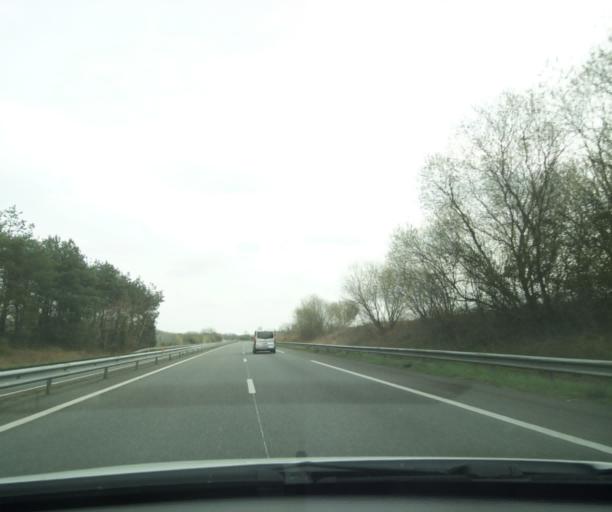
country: FR
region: Aquitaine
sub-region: Departement des Landes
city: Peyrehorade
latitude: 43.5203
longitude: -1.1326
